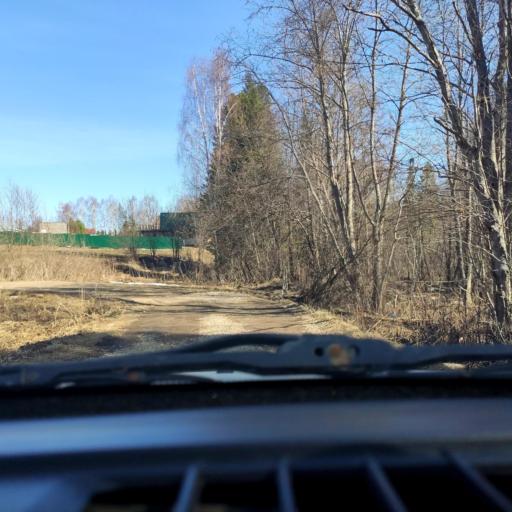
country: RU
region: Perm
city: Kultayevo
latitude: 57.8269
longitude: 55.7853
